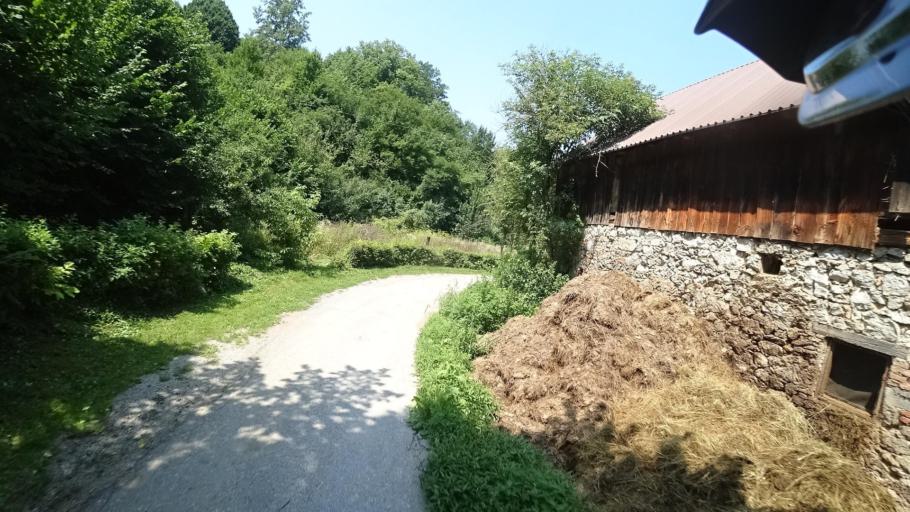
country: HR
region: Karlovacka
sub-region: Grad Ogulin
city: Ogulin
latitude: 45.3117
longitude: 15.1757
